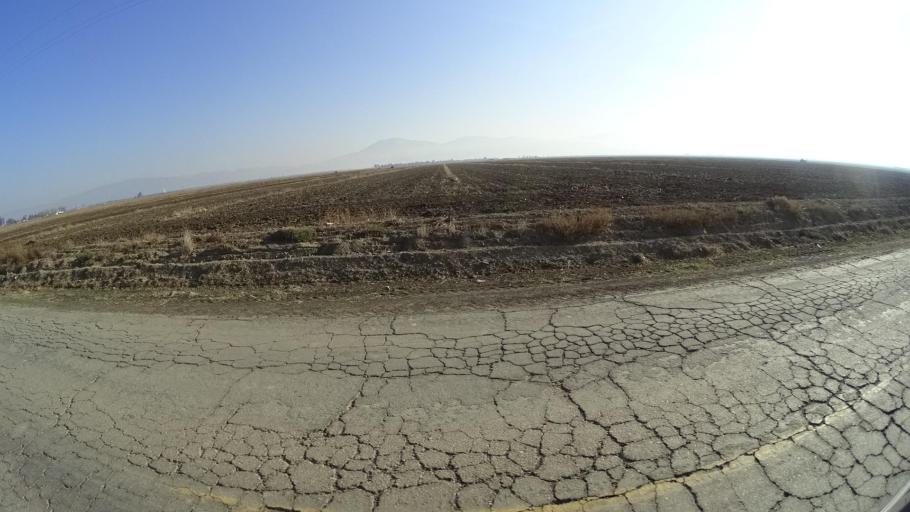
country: US
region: California
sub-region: Kern County
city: Weedpatch
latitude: 35.1752
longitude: -118.9678
